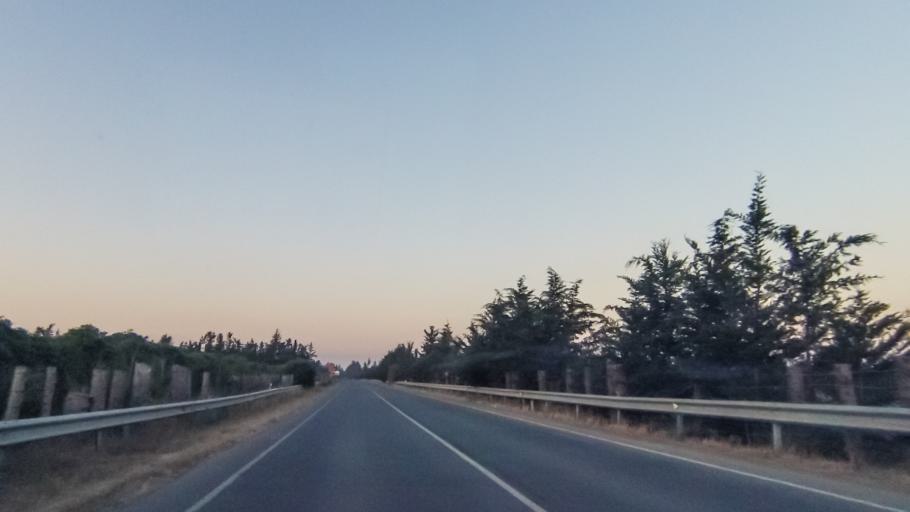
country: CY
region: Limassol
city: Ypsonas
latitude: 34.6479
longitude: 32.9769
